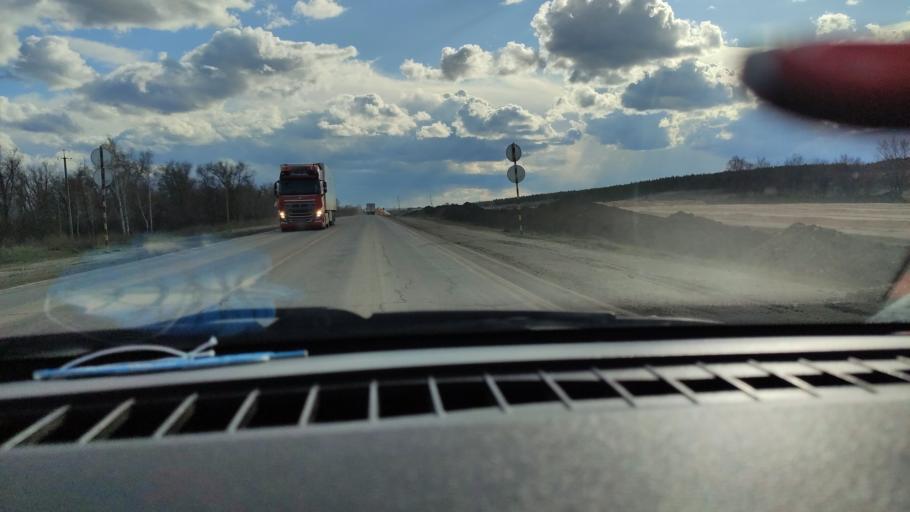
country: RU
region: Saratov
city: Sinodskoye
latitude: 52.0161
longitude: 46.6984
